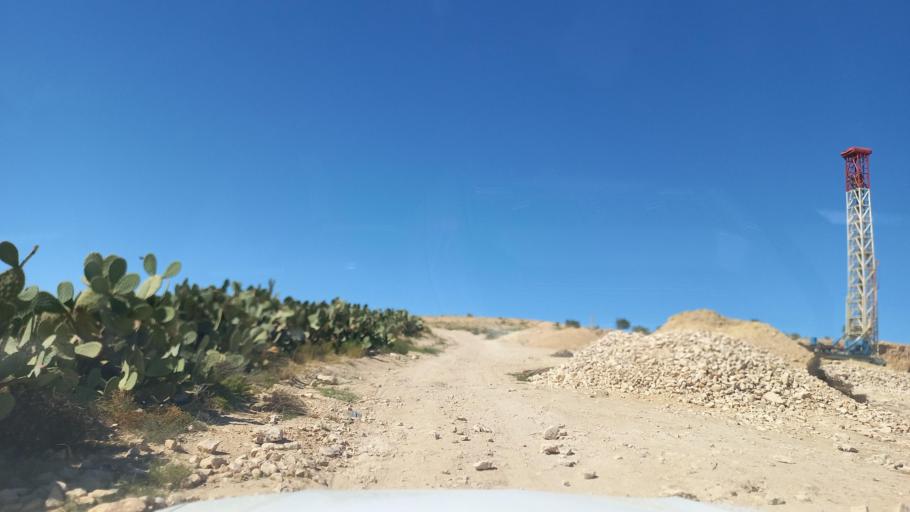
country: TN
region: Al Qasrayn
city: Sbiba
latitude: 35.3755
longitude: 9.0801
